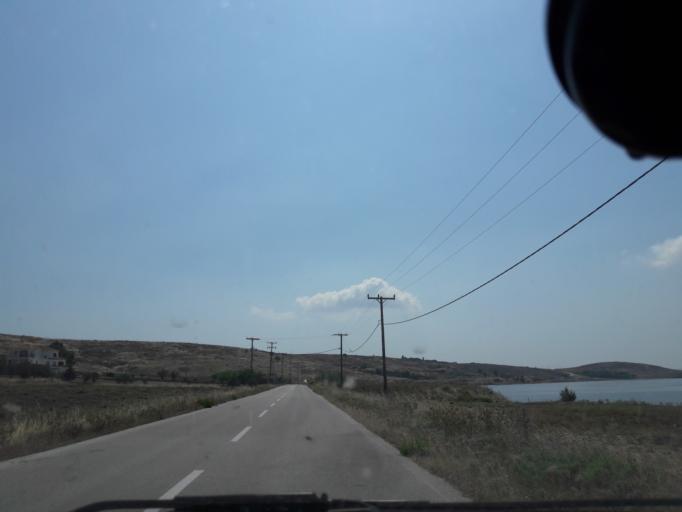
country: GR
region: North Aegean
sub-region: Nomos Lesvou
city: Myrina
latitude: 39.8616
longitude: 25.2617
